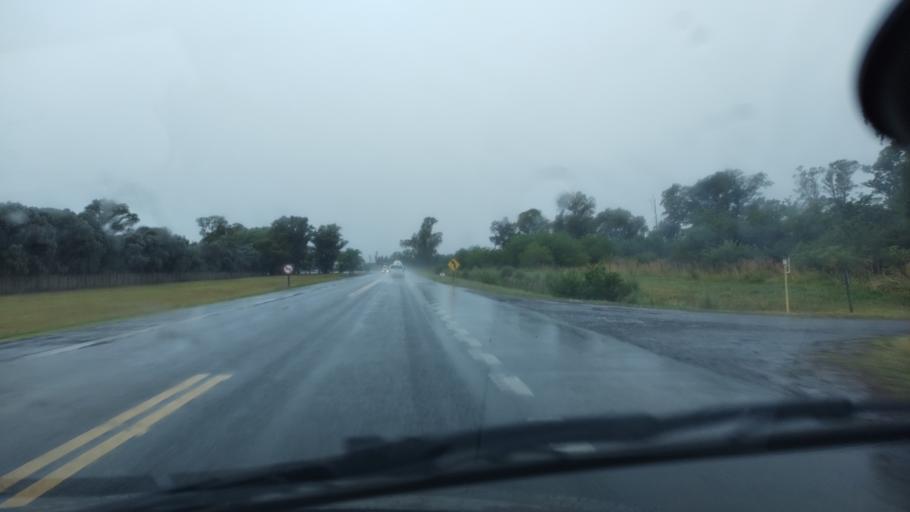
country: AR
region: Buenos Aires
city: Canuelas
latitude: -35.0541
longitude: -58.7813
